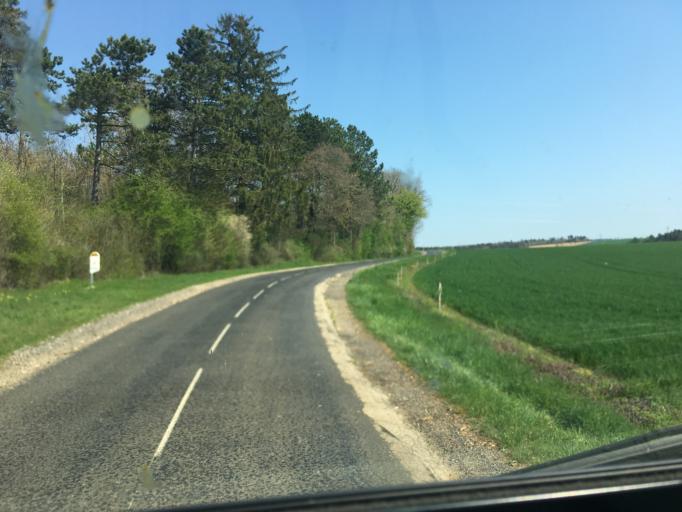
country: FR
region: Lorraine
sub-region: Departement de Meurthe-et-Moselle
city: Montauville
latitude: 48.9059
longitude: 5.9198
